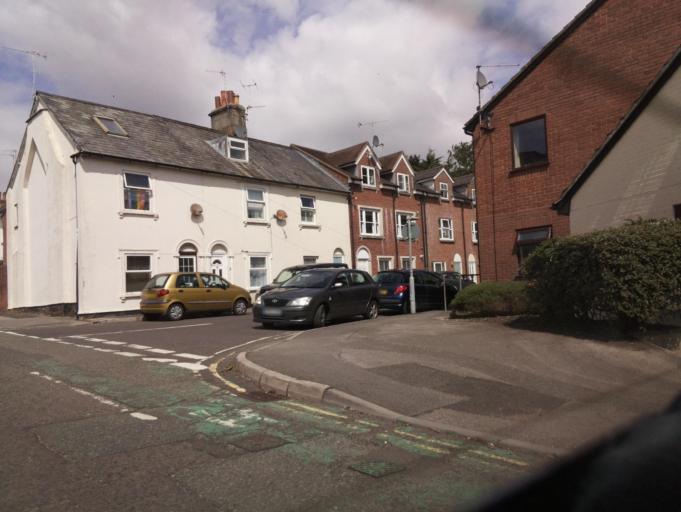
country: GB
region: England
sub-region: Dorset
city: Blandford Forum
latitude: 50.8577
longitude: -2.1609
